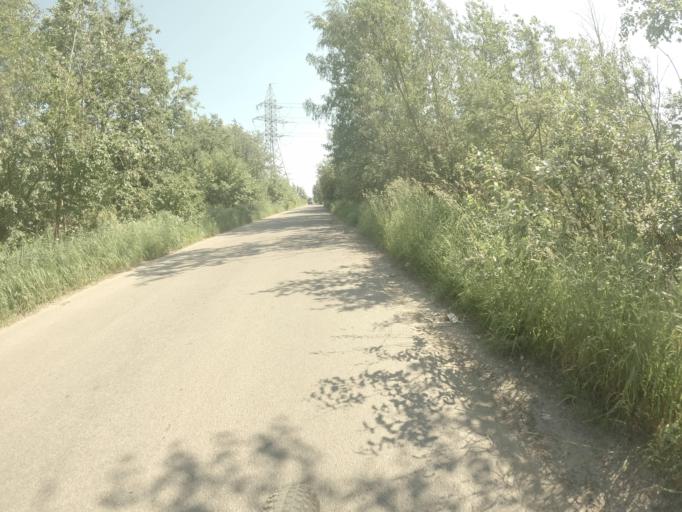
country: RU
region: St.-Petersburg
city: Obukhovo
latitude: 59.8393
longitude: 30.4699
